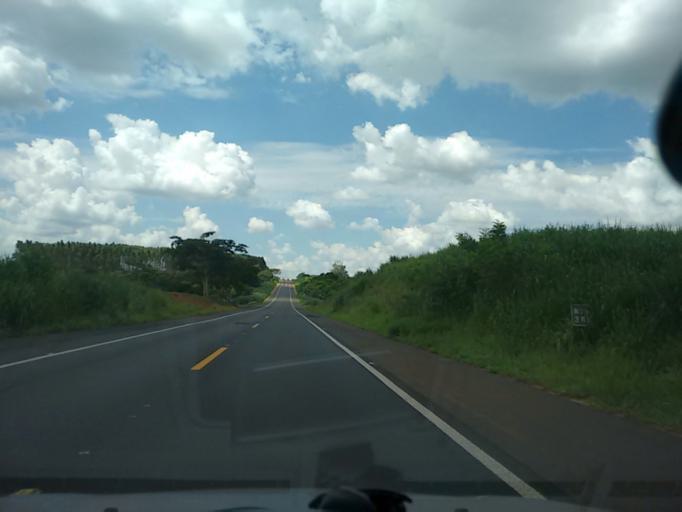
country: BR
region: Sao Paulo
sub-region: Osvaldo Cruz
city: Osvaldo Cruz
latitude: -21.8407
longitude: -50.8279
